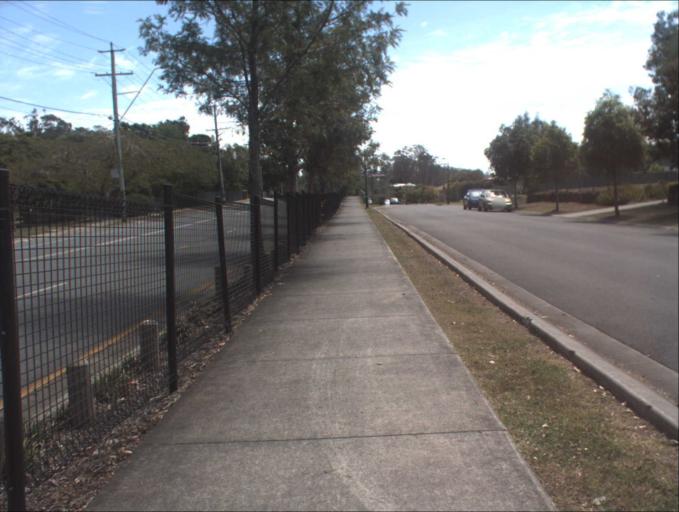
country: AU
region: Queensland
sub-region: Logan
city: Slacks Creek
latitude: -27.6345
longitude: 153.1552
